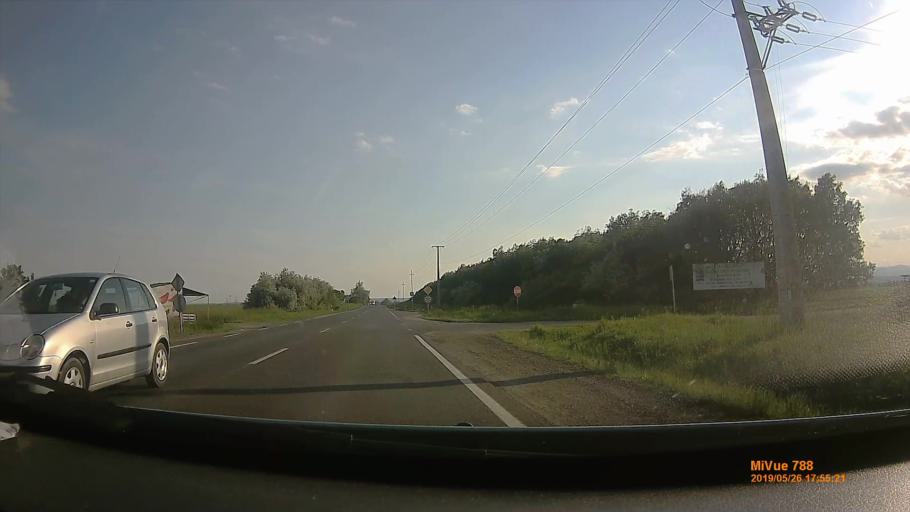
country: HU
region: Borsod-Abauj-Zemplen
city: Arnot
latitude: 48.1300
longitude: 20.8755
